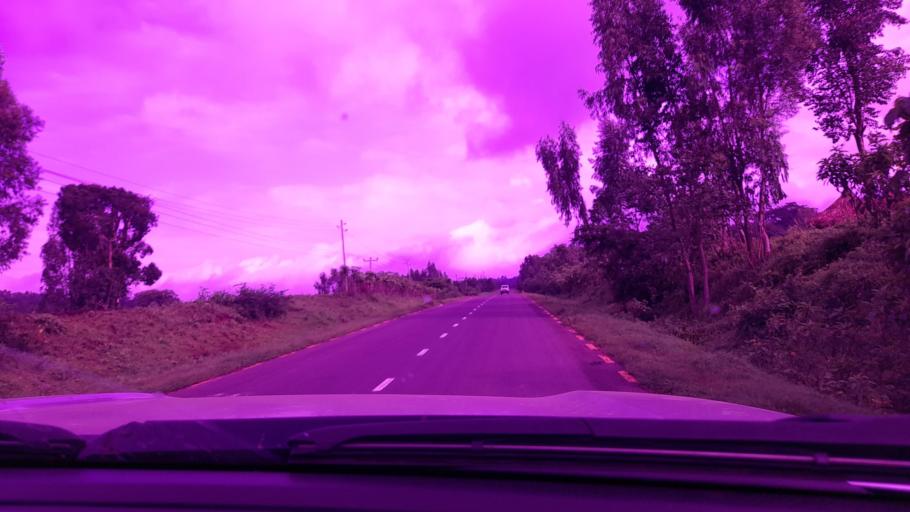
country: ET
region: Oromiya
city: Bedele
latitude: 8.2347
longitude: 36.4492
